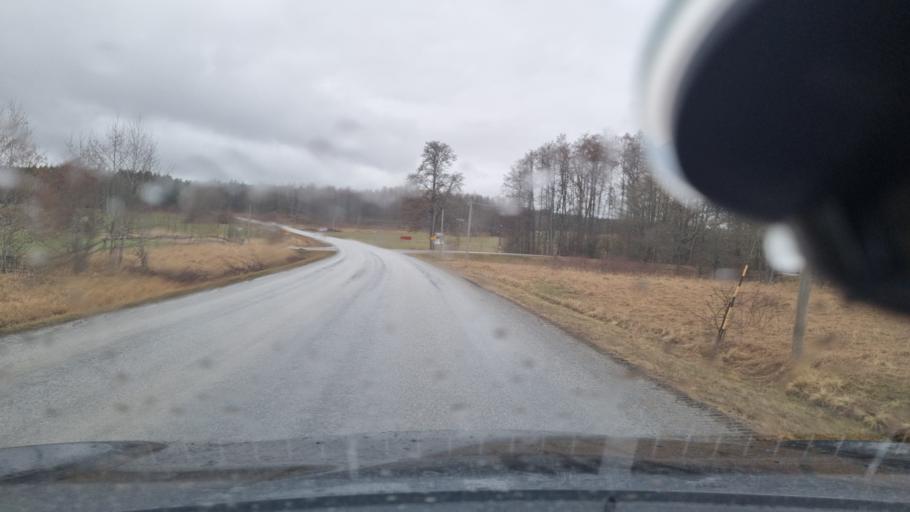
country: SE
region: Stockholm
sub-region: Sigtuna Kommun
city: Sigtuna
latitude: 59.5484
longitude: 17.7376
